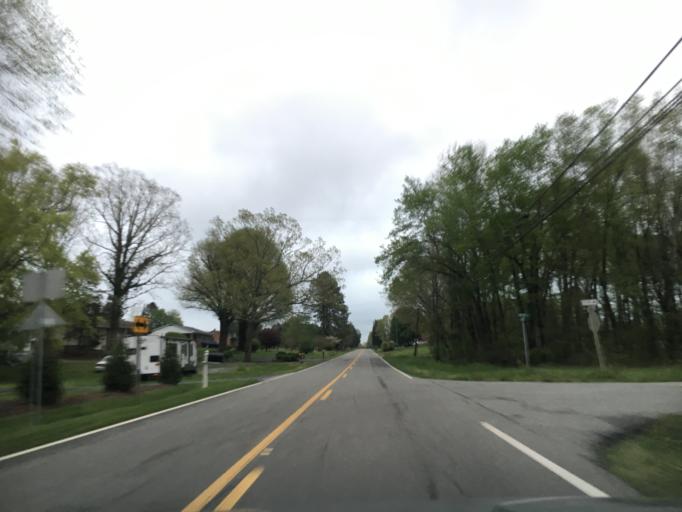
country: US
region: Virginia
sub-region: Halifax County
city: South Boston
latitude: 36.6549
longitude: -78.8761
